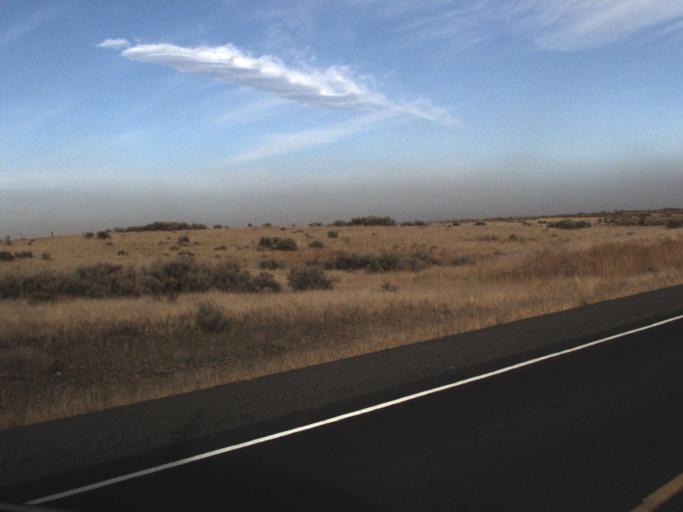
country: US
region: Washington
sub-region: Adams County
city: Ritzville
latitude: 47.3129
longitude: -118.7693
